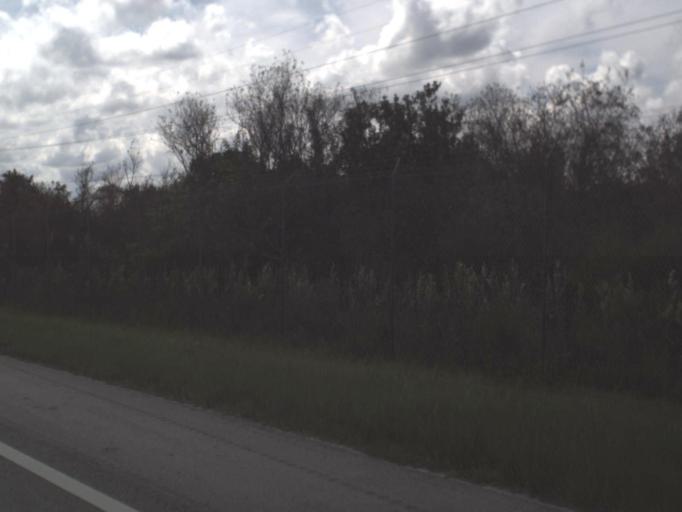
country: US
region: Florida
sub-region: Collier County
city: Immokalee
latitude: 26.1612
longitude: -81.3453
